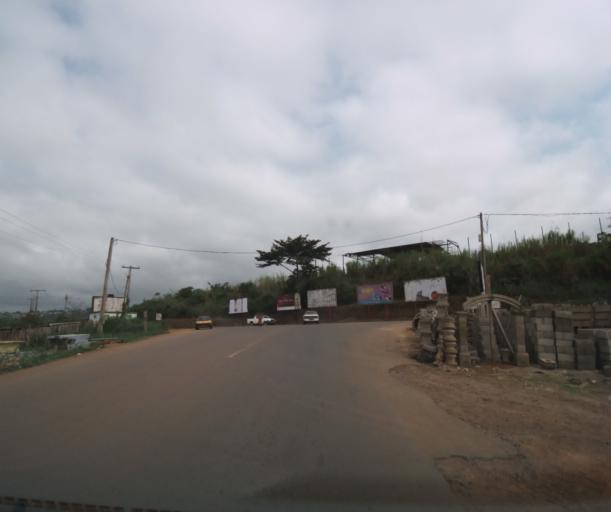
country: CM
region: Centre
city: Yaounde
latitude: 3.8071
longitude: 11.5189
